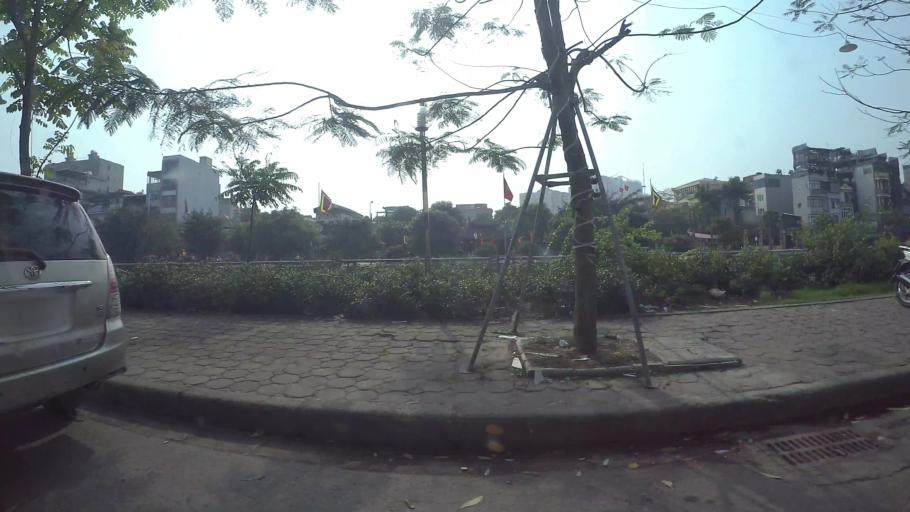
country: VN
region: Ha Noi
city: Thanh Xuan
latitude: 20.9900
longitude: 105.8136
